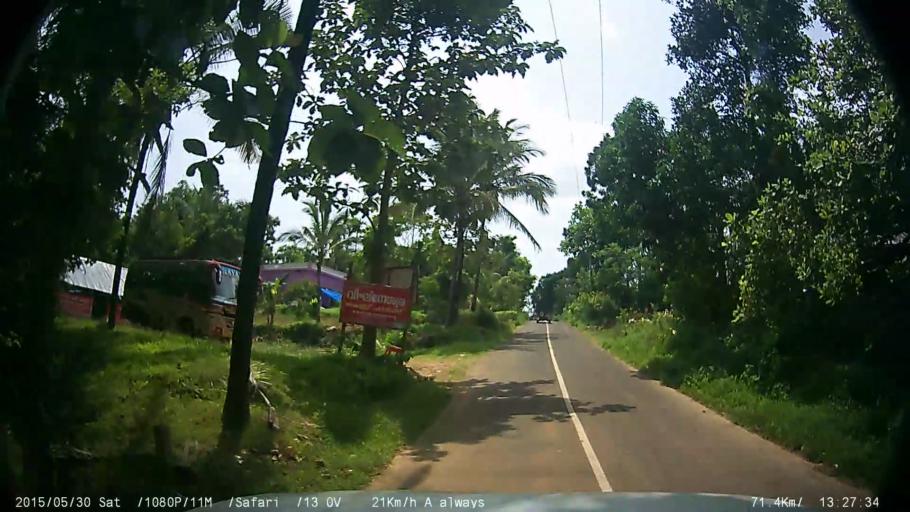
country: IN
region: Kerala
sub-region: Wayanad
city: Panamaram
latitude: 11.8219
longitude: 76.0875
